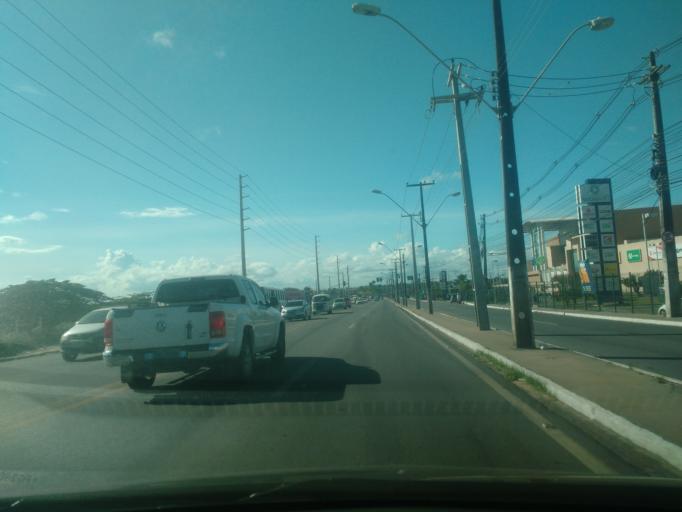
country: BR
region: Alagoas
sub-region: Satuba
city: Satuba
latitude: -9.5602
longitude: -35.7467
